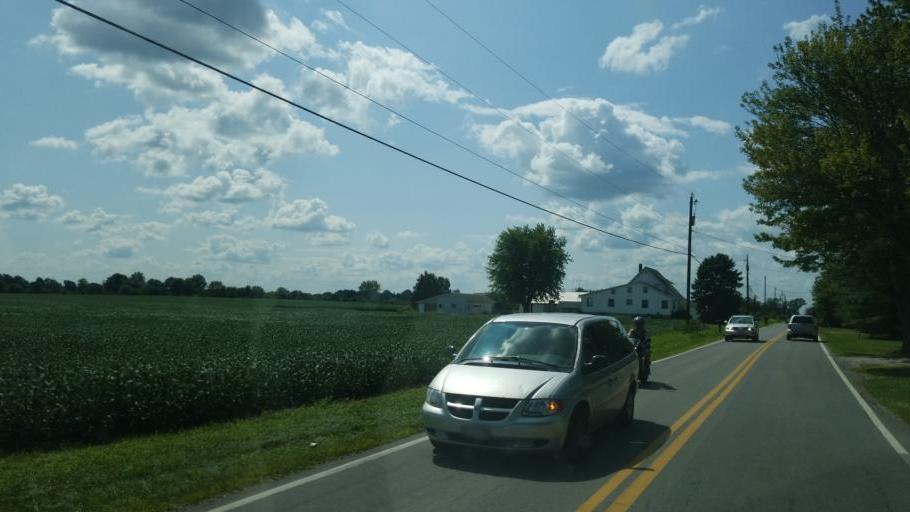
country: US
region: Ohio
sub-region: Delaware County
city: Lewis Center
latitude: 40.2263
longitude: -83.0071
